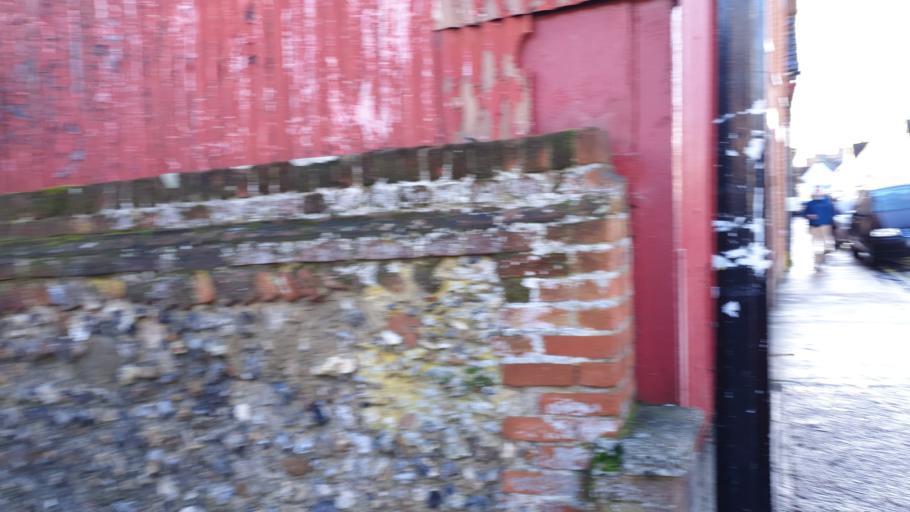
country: GB
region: England
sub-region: Suffolk
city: Hadleigh
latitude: 52.0444
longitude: 0.9560
